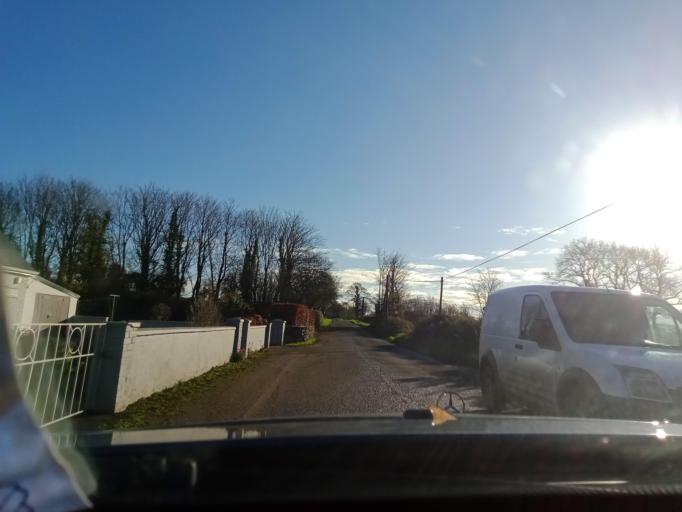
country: IE
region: Leinster
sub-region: Kilkenny
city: Mooncoin
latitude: 52.3393
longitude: -7.2676
